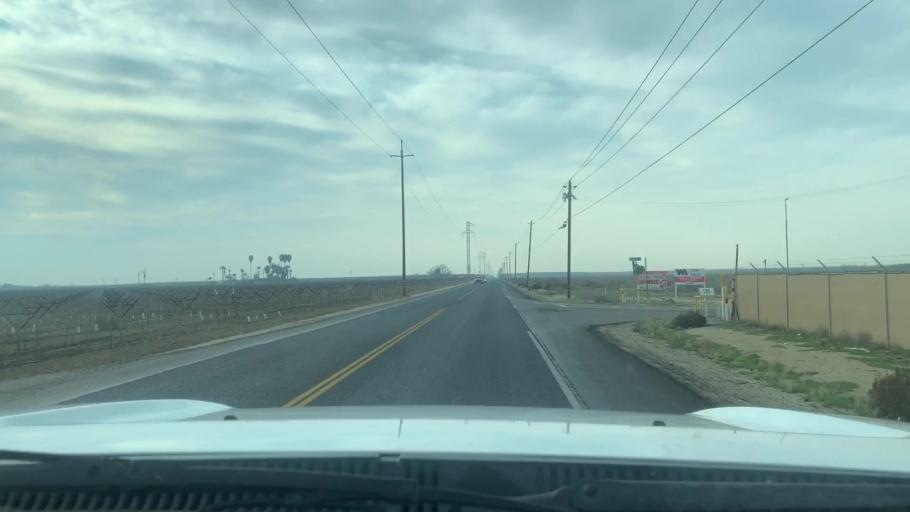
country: US
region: California
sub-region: Kern County
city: Shafter
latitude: 35.4418
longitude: -119.2786
